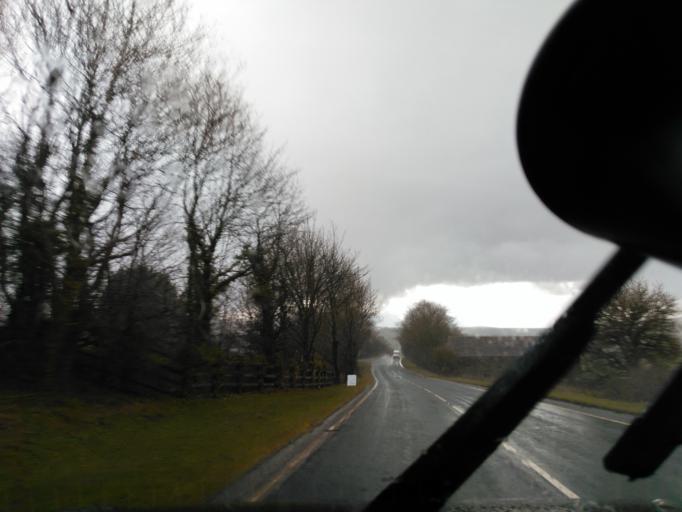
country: GB
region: England
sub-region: North Yorkshire
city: Embsay
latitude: 53.9730
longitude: -1.9693
